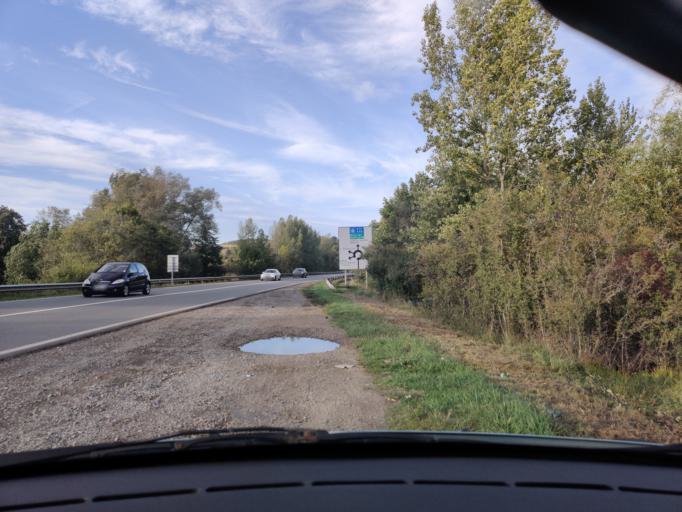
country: FR
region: Auvergne
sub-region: Departement du Puy-de-Dome
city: Mozac
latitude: 45.8936
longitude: 3.0724
